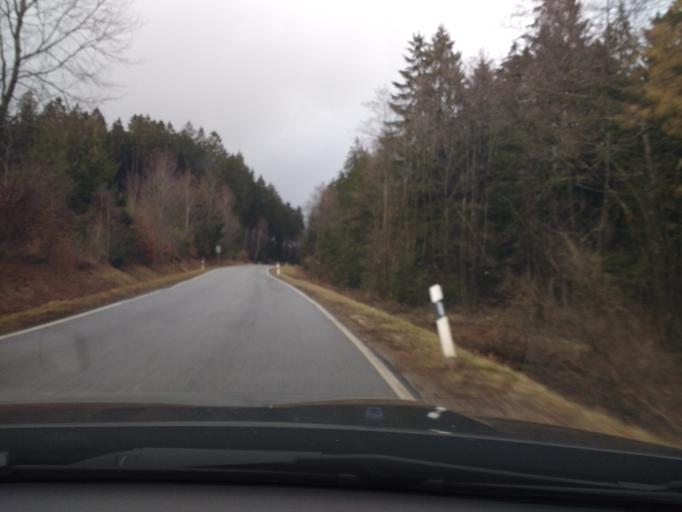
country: DE
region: Rheinland-Pfalz
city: Greimerath
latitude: 49.5742
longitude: 6.7118
